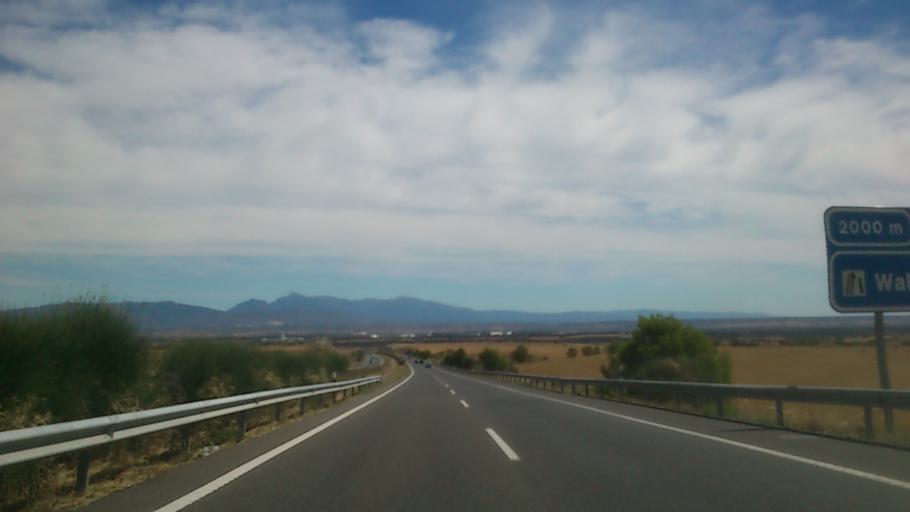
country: ES
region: Aragon
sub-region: Provincia de Huesca
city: Sangarren
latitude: 42.0751
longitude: -0.4988
